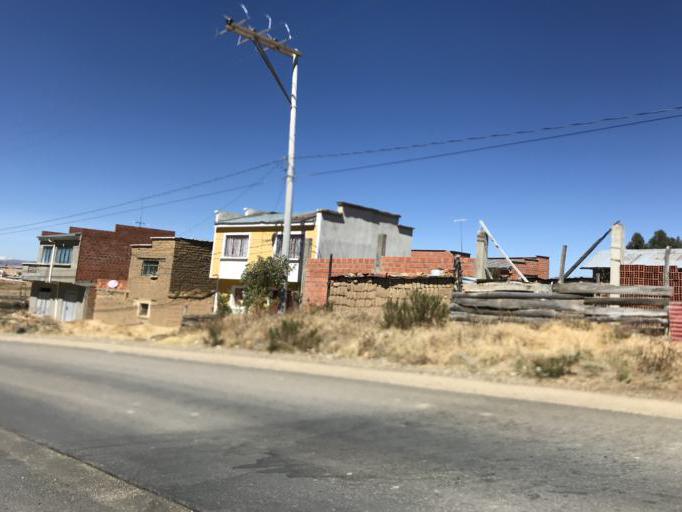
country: BO
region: La Paz
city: Huatajata
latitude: -16.2107
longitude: -68.6968
